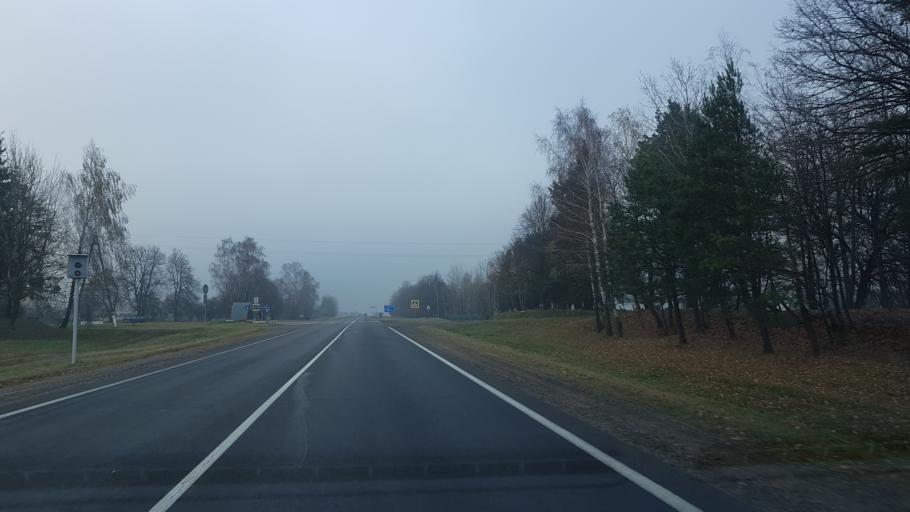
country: BY
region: Mogilev
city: Babruysk
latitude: 53.1771
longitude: 29.3453
